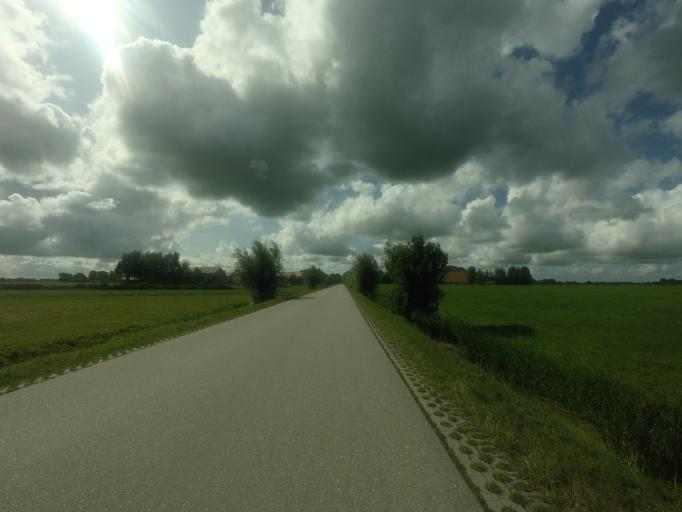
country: NL
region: Friesland
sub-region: Gemeente Littenseradiel
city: Makkum
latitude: 53.0905
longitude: 5.7031
